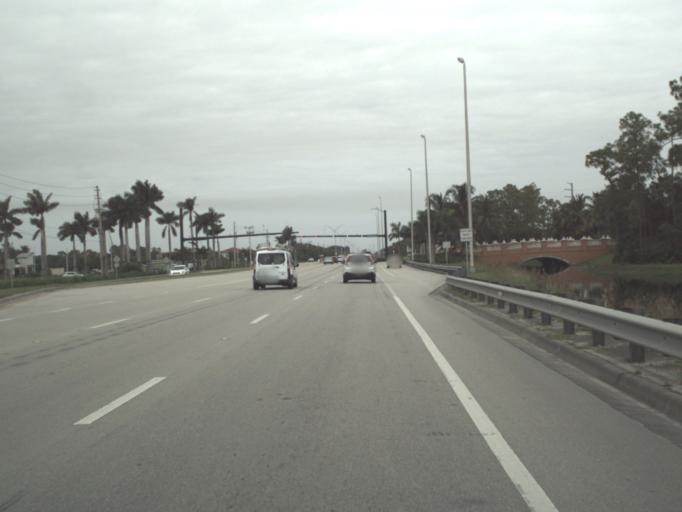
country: US
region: Florida
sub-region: Collier County
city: Lely Resort
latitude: 26.0856
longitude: -81.6873
